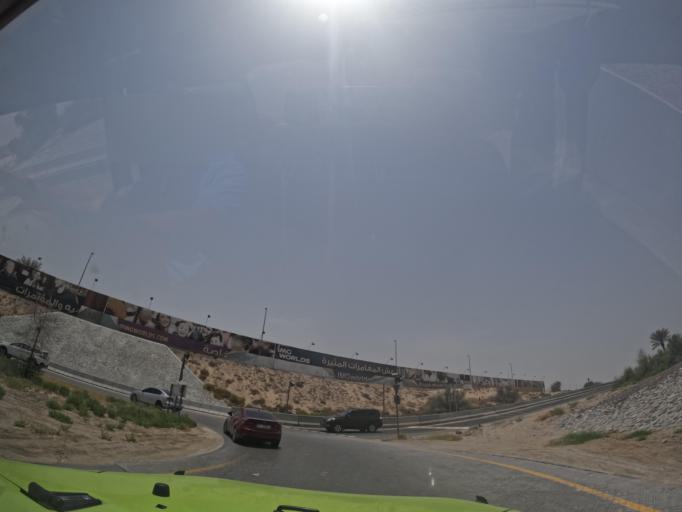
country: AE
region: Dubai
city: Dubai
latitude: 25.0899
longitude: 55.3242
